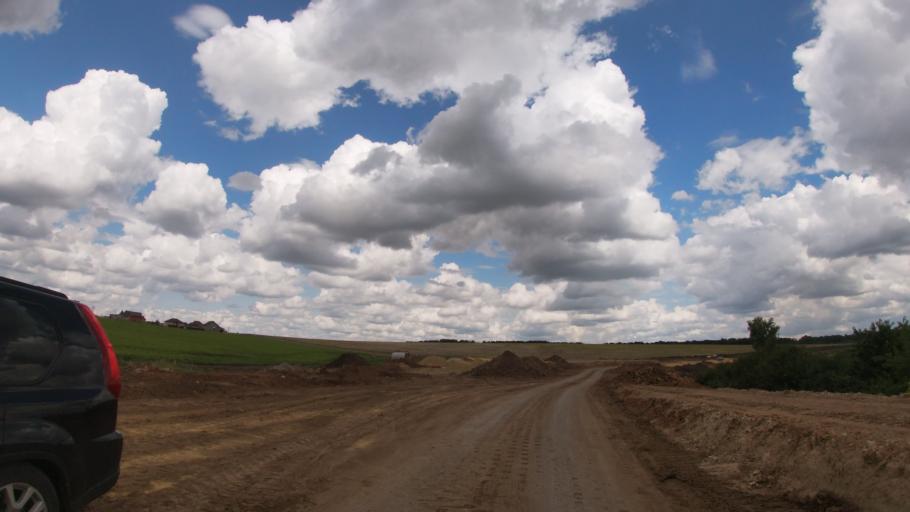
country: RU
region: Belgorod
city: Mayskiy
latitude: 50.5172
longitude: 36.4918
